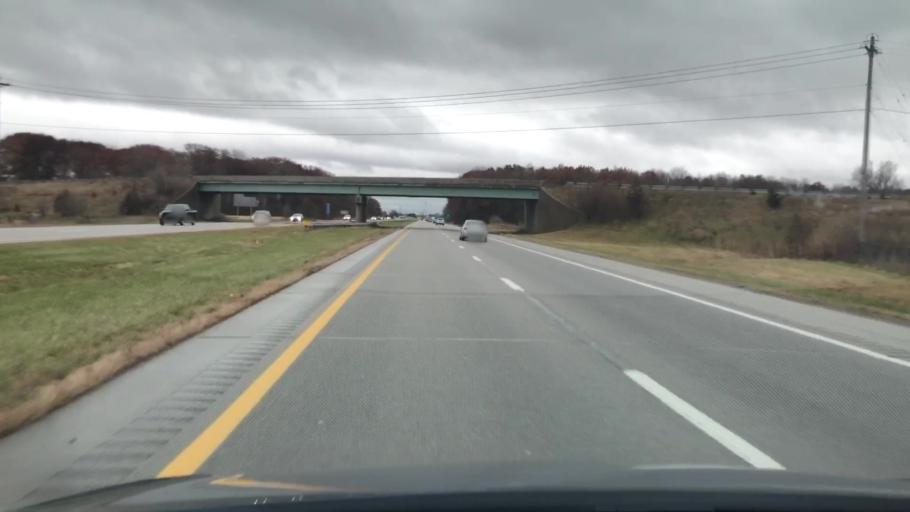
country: US
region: Ohio
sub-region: Wood County
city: Walbridge
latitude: 41.5740
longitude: -83.4692
